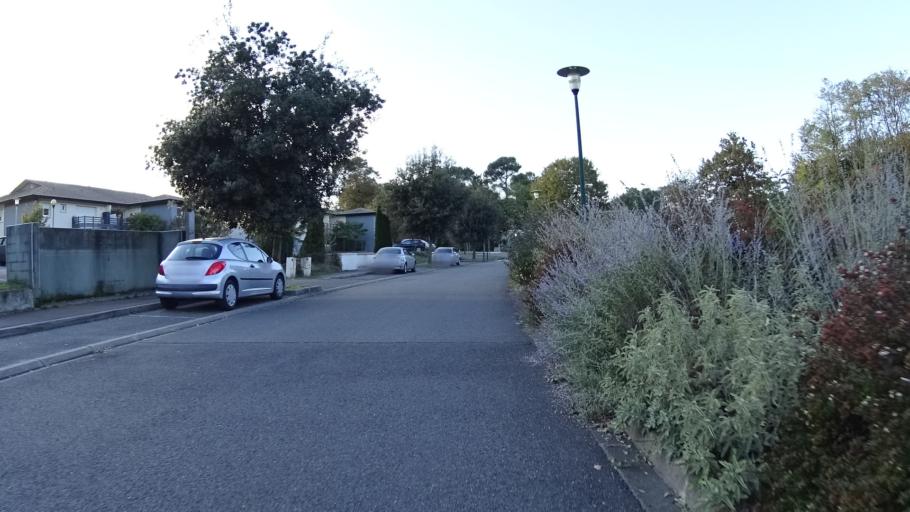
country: FR
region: Aquitaine
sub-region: Departement des Landes
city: Saint-Paul-les-Dax
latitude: 43.7367
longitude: -1.0478
